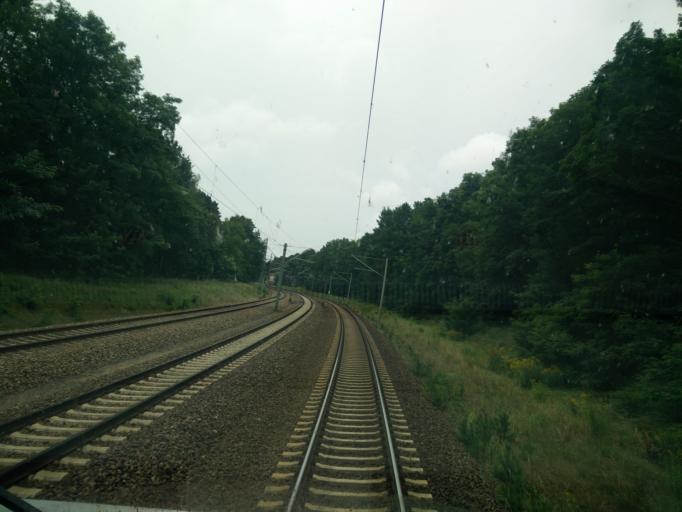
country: DE
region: Brandenburg
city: Halbe
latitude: 52.0362
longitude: 13.7185
